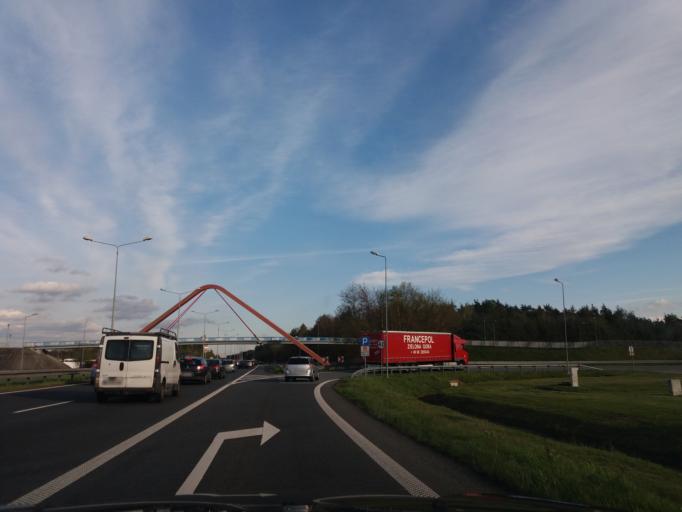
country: PL
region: Opole Voivodeship
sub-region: Powiat opolski
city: Niemodlin
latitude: 50.6780
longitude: 17.6516
